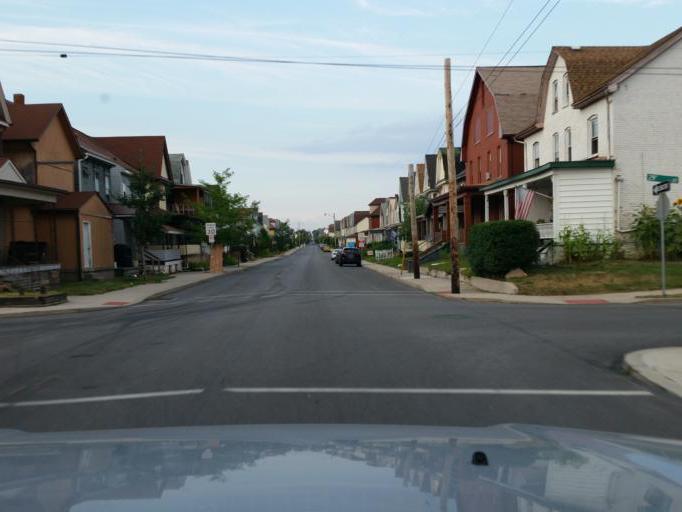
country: US
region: Pennsylvania
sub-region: Blair County
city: Altoona
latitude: 40.4970
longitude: -78.4100
